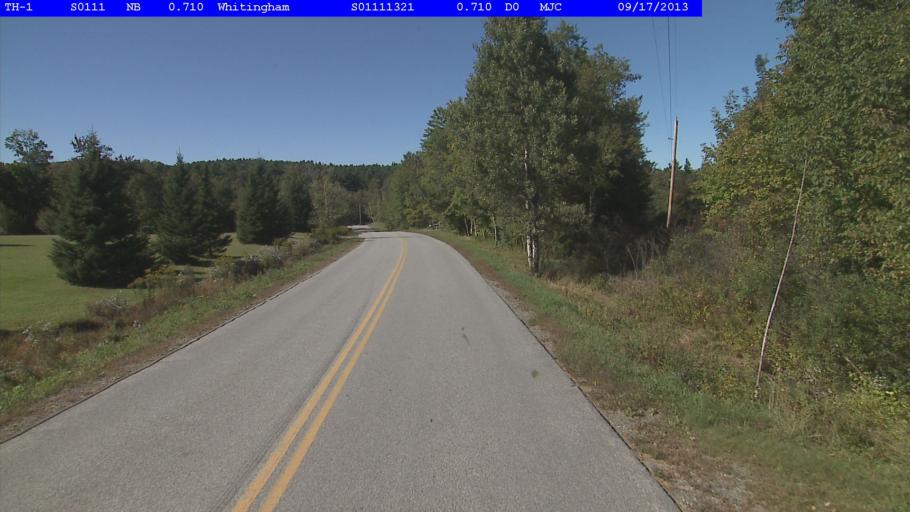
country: US
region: Massachusetts
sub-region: Franklin County
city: Charlemont
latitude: 42.7468
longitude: -72.8162
